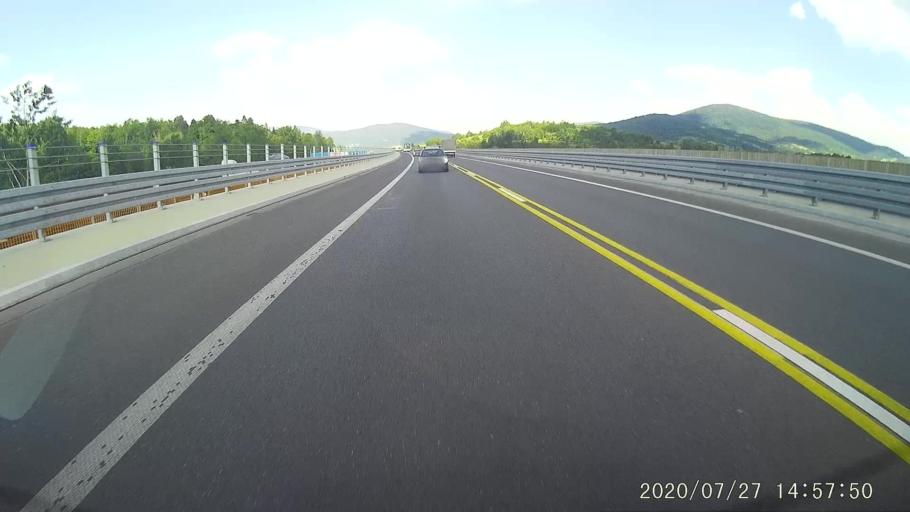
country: PL
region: Lesser Poland Voivodeship
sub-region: Powiat myslenicki
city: Krzczonow
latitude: 49.6961
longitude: 19.9378
